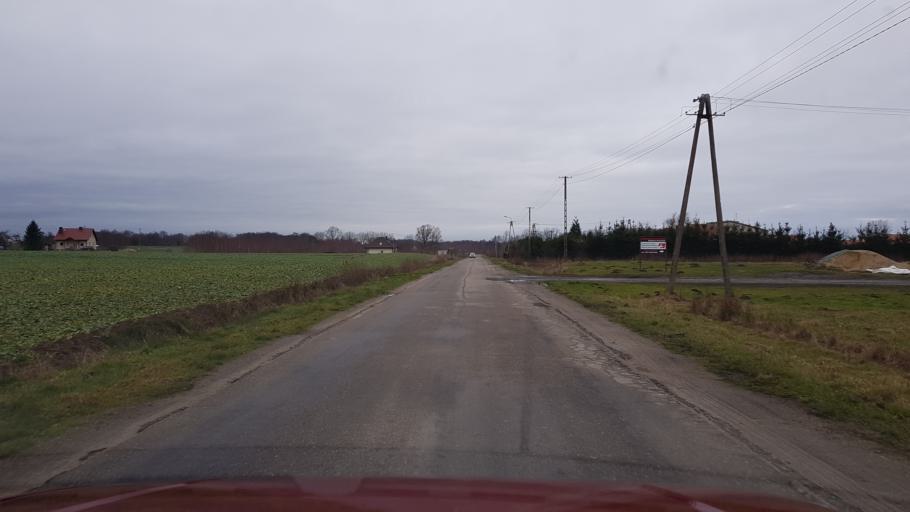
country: PL
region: West Pomeranian Voivodeship
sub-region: Powiat koszalinski
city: Mielno
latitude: 54.1898
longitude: 16.0351
